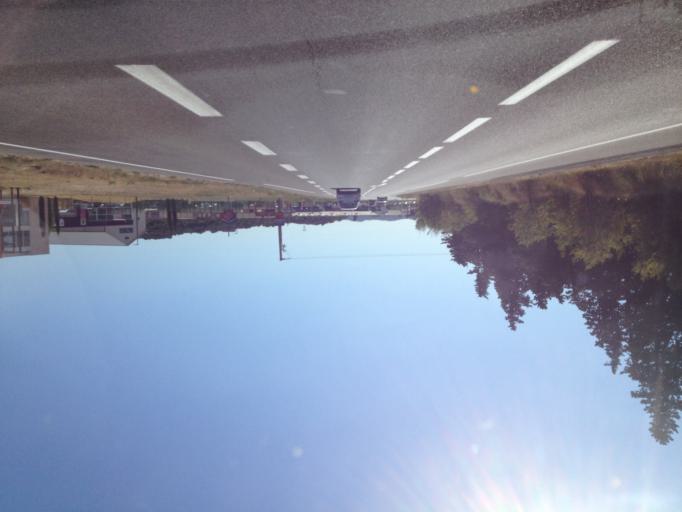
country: FR
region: Provence-Alpes-Cote d'Azur
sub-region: Departement du Vaucluse
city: Piolenc
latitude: 44.1639
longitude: 4.7796
